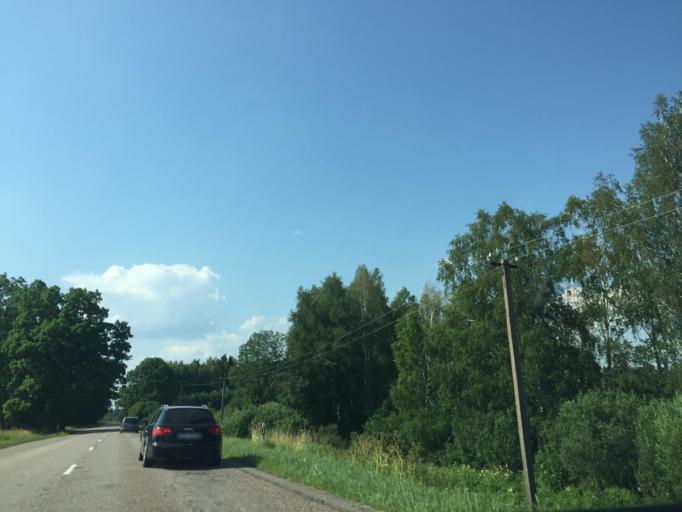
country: LV
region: Limbazu Rajons
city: Limbazi
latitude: 57.4887
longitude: 24.8556
